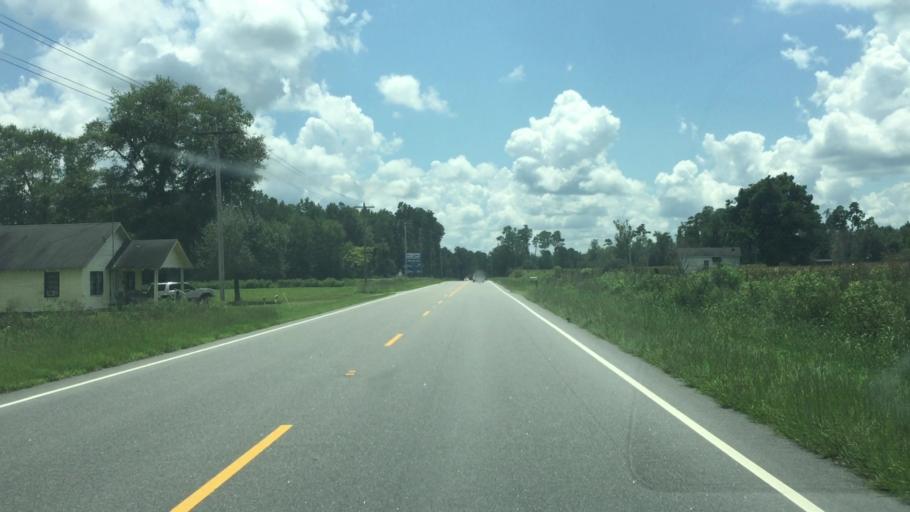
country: US
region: North Carolina
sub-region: Columbus County
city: Tabor City
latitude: 34.2212
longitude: -78.8241
